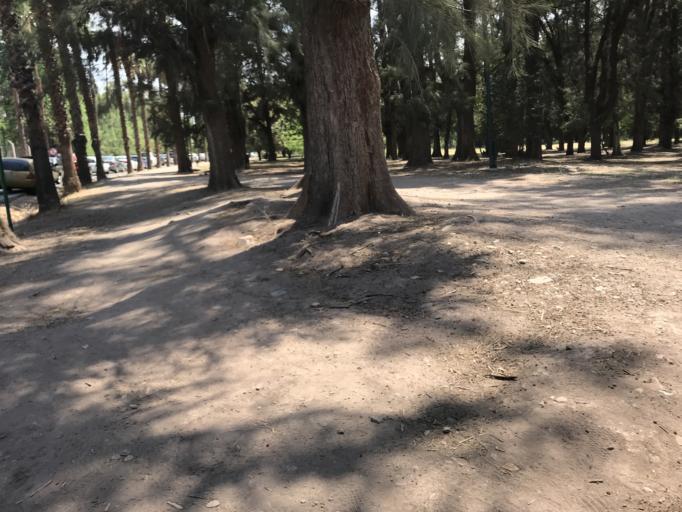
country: AR
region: Mendoza
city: Mendoza
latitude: -32.8940
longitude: -68.8676
